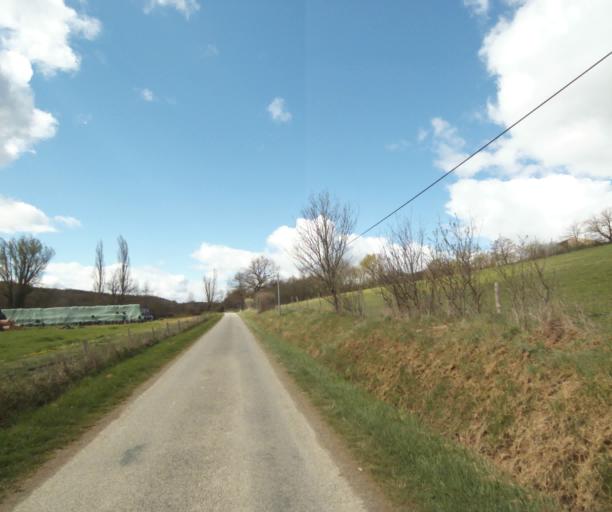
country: FR
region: Midi-Pyrenees
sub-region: Departement de l'Ariege
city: Saverdun
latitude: 43.1919
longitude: 1.5646
